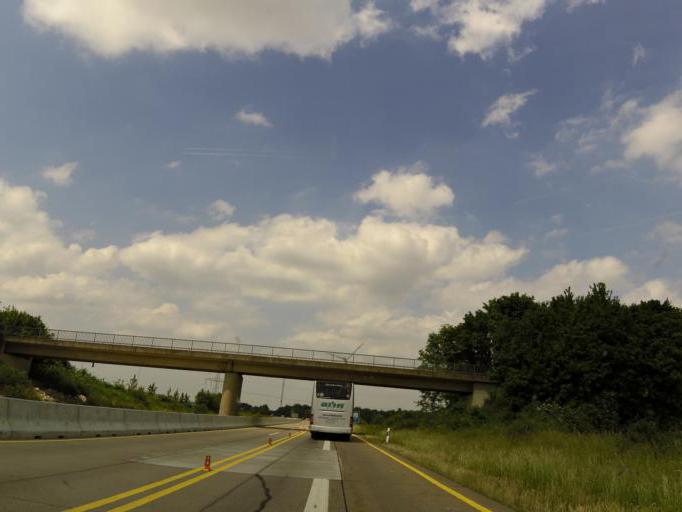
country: DE
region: Bavaria
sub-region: Regierungsbezirk Mittelfranken
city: Uffenheim
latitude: 49.5216
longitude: 10.1951
